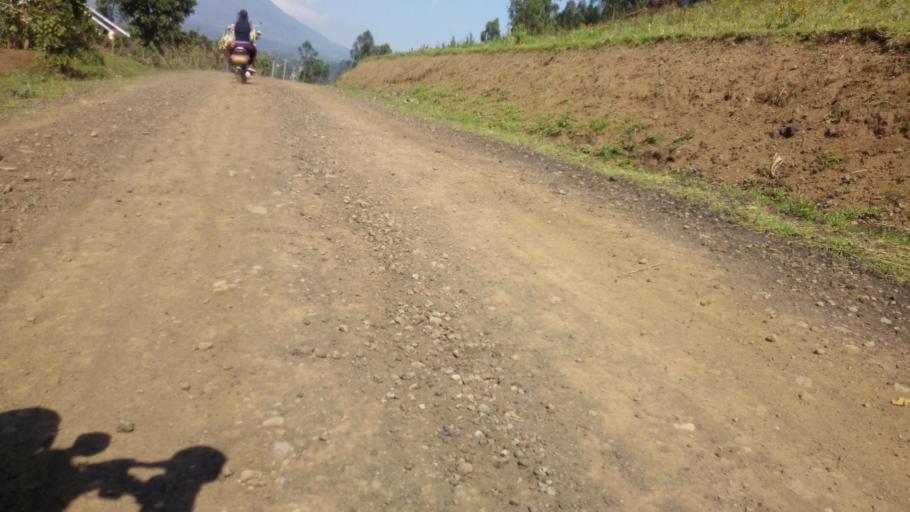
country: UG
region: Western Region
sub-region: Kisoro District
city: Kisoro
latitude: -1.3404
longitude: 29.6324
